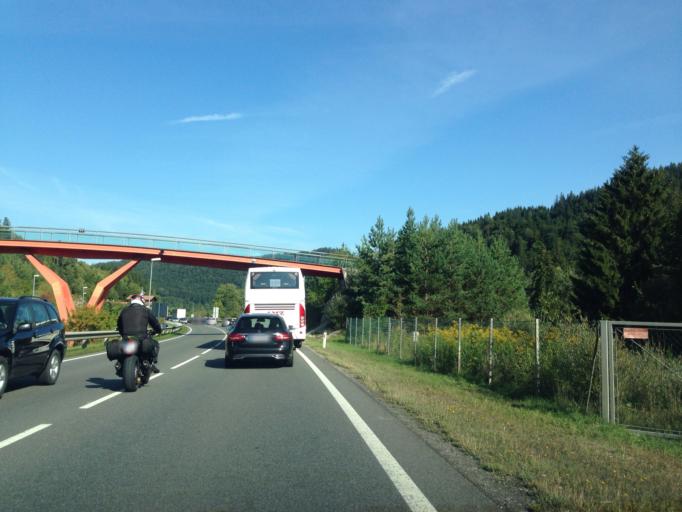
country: AT
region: Tyrol
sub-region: Politischer Bezirk Reutte
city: Musau
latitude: 47.5423
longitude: 10.6653
